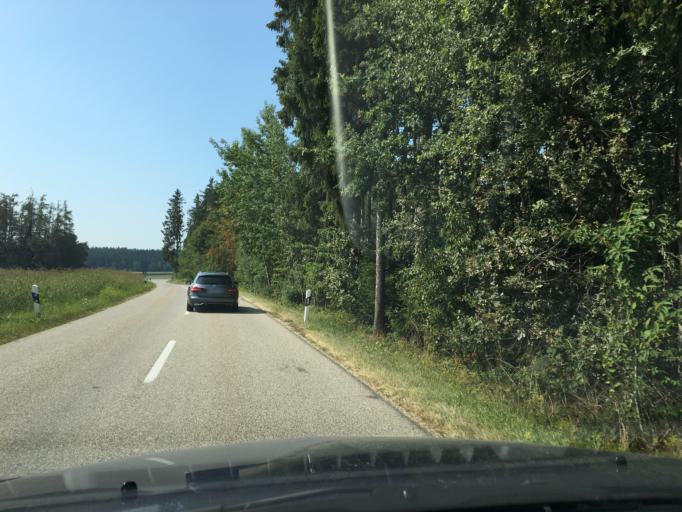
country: DE
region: Bavaria
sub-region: Upper Bavaria
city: Niederbergkirchen
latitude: 48.3308
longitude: 12.4825
